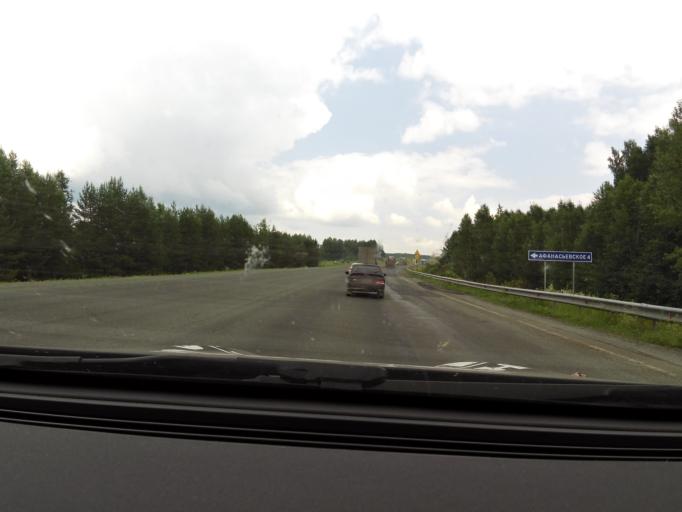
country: RU
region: Sverdlovsk
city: Ufimskiy
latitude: 56.7826
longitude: 58.2675
